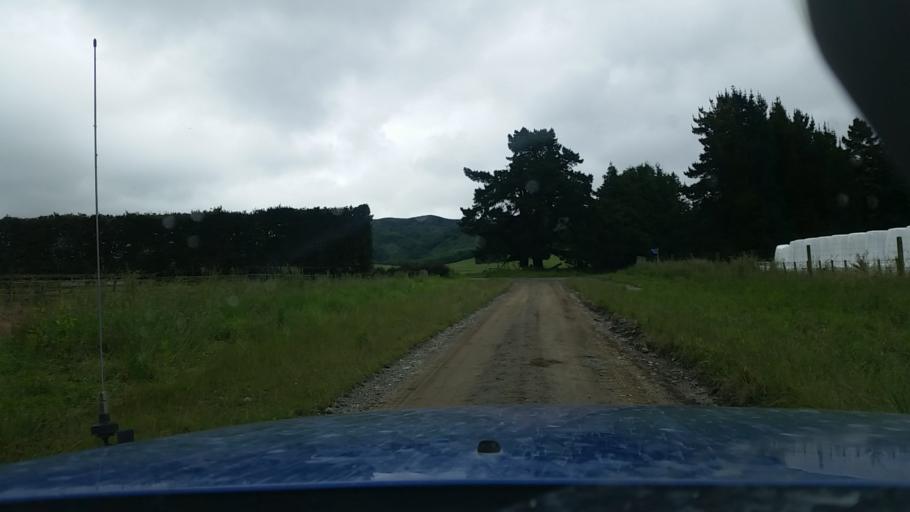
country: NZ
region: Canterbury
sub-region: Ashburton District
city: Methven
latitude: -43.6641
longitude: 171.4141
